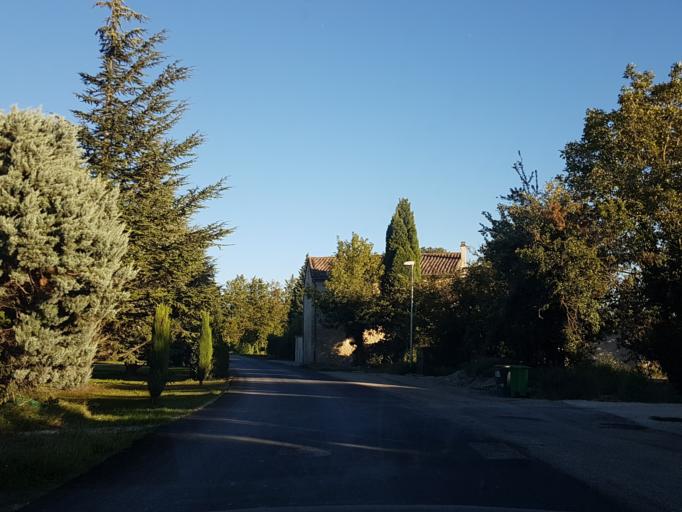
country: FR
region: Provence-Alpes-Cote d'Azur
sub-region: Departement du Vaucluse
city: Velleron
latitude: 43.9562
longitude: 5.0336
